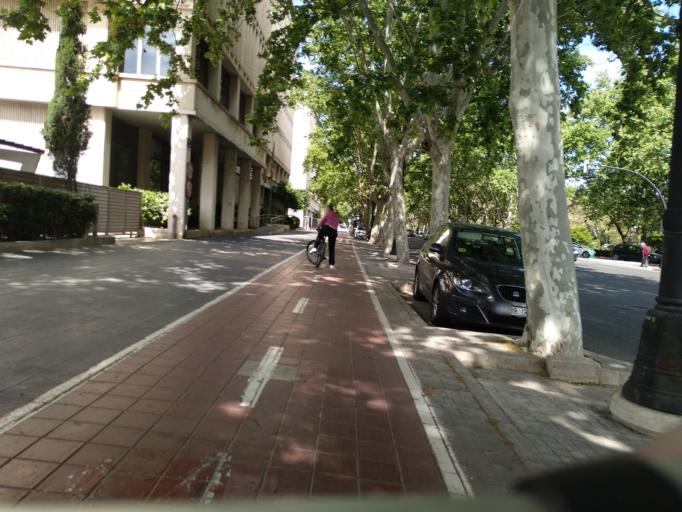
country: ES
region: Valencia
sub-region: Provincia de Valencia
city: Valencia
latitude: 39.4760
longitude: -0.3562
